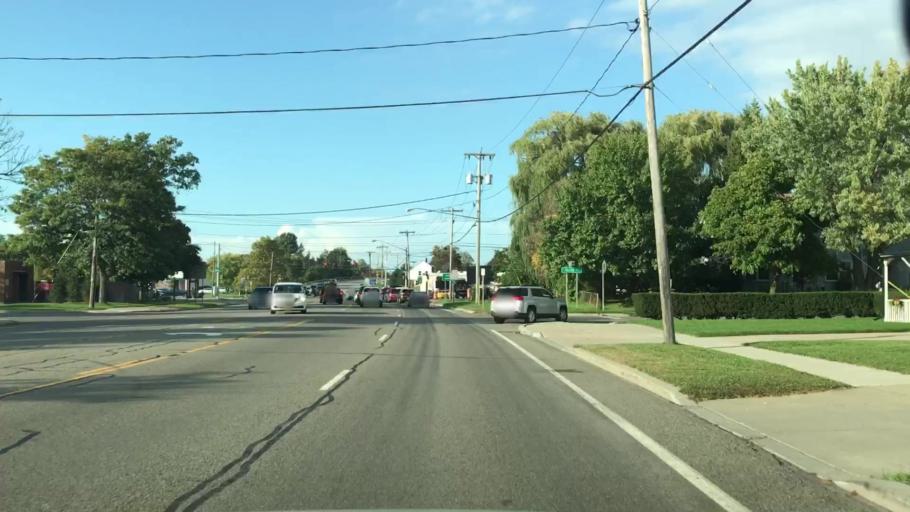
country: US
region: New York
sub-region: Erie County
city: Williamsville
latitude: 42.9483
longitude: -78.7543
